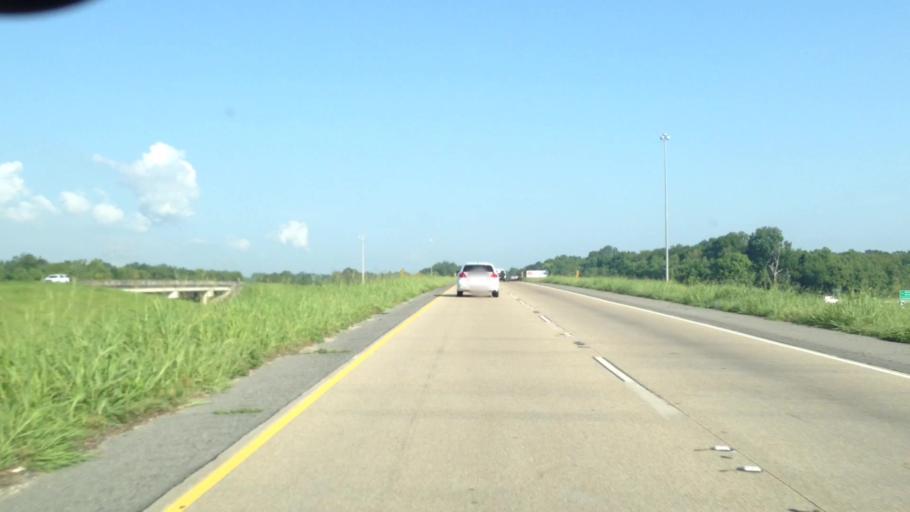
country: US
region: Louisiana
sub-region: Ascension Parish
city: Gonzales
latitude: 30.1917
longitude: -90.9181
